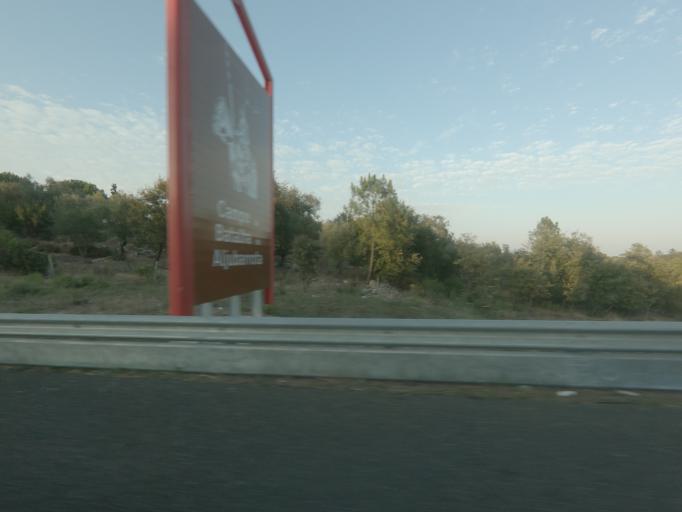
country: PT
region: Leiria
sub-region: Leiria
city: Santa Catarina da Serra
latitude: 39.6926
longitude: -8.6919
